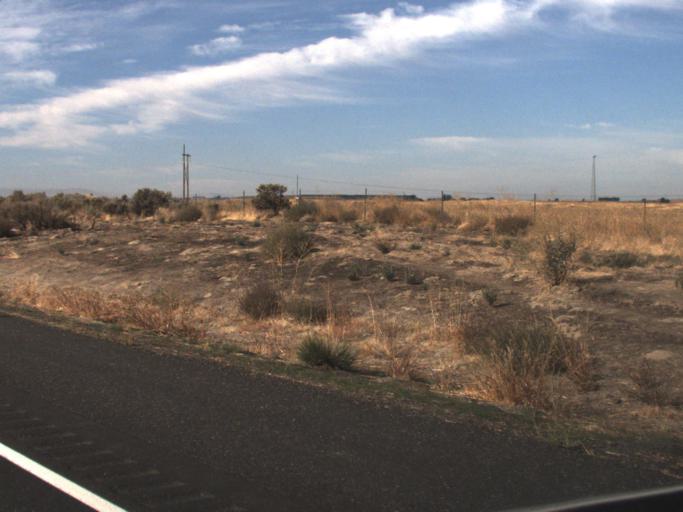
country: US
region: Washington
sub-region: Franklin County
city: Connell
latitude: 46.5757
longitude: -118.9818
